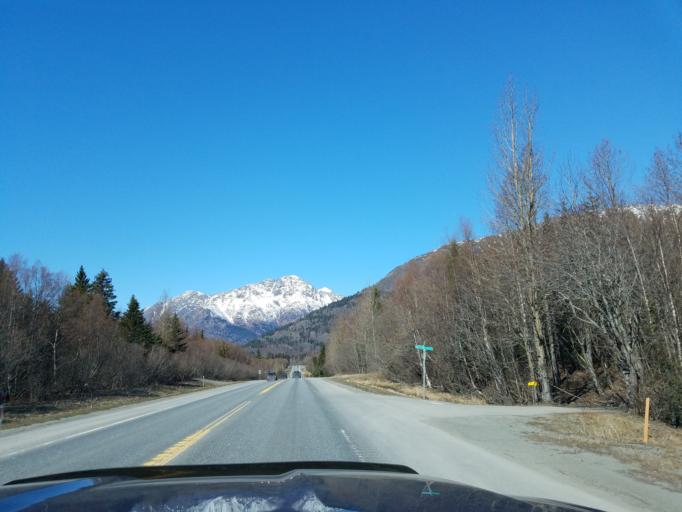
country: US
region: Alaska
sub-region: Anchorage Municipality
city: Girdwood
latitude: 60.9636
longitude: -149.4358
